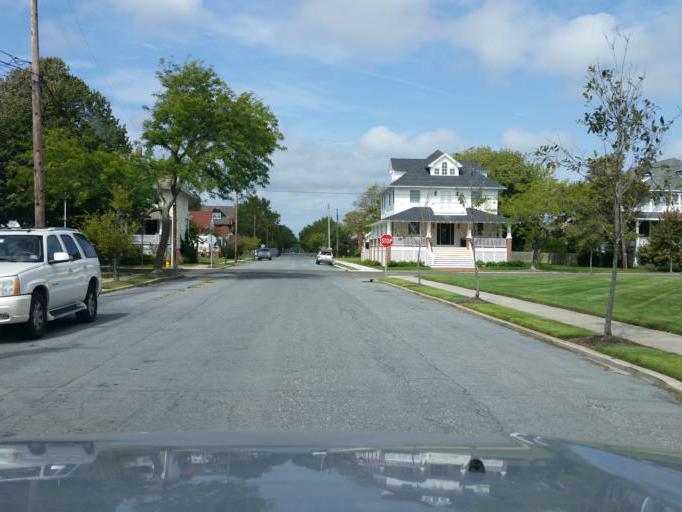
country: US
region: New Jersey
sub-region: Cape May County
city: Cape May
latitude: 38.9355
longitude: -74.9041
